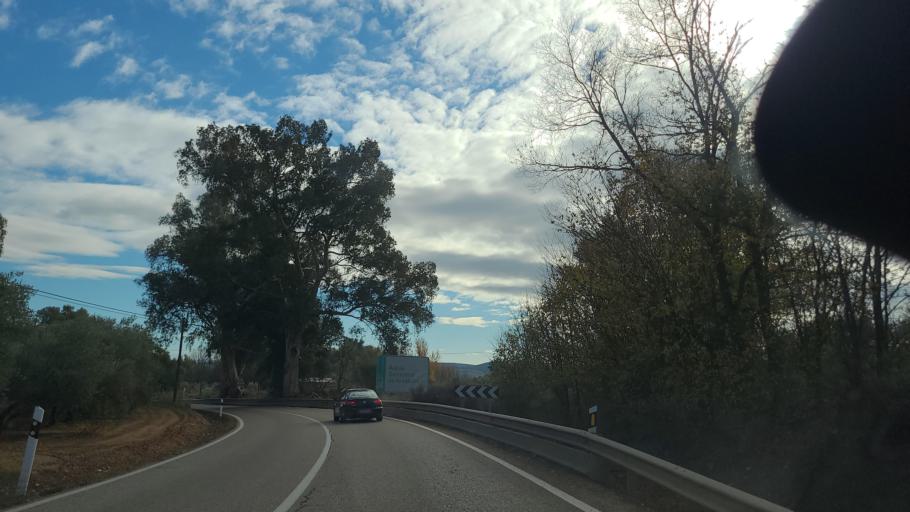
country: ES
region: Andalusia
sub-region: Provincia de Jaen
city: Villanueva de la Reina
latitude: 38.0292
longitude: -3.9179
